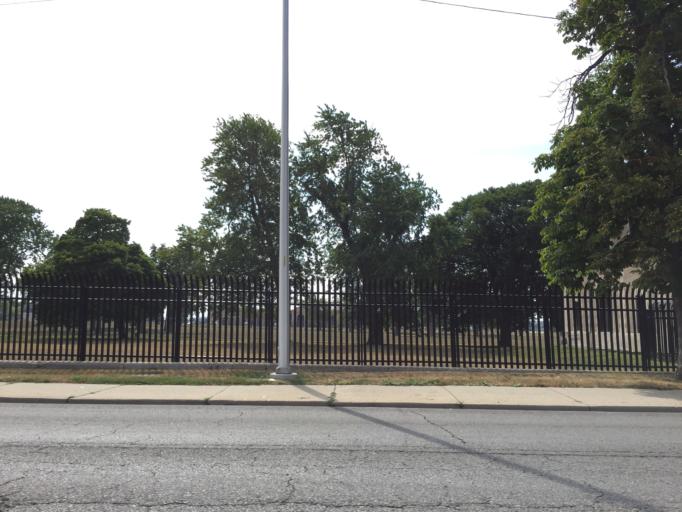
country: US
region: Michigan
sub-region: Wayne County
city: Grosse Pointe Park
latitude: 42.3604
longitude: -82.9822
